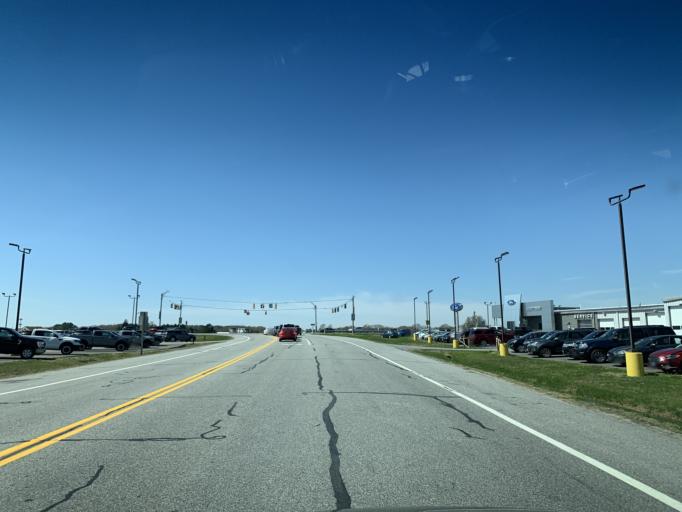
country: US
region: Maryland
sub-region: Talbot County
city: Easton
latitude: 38.8125
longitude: -76.0585
